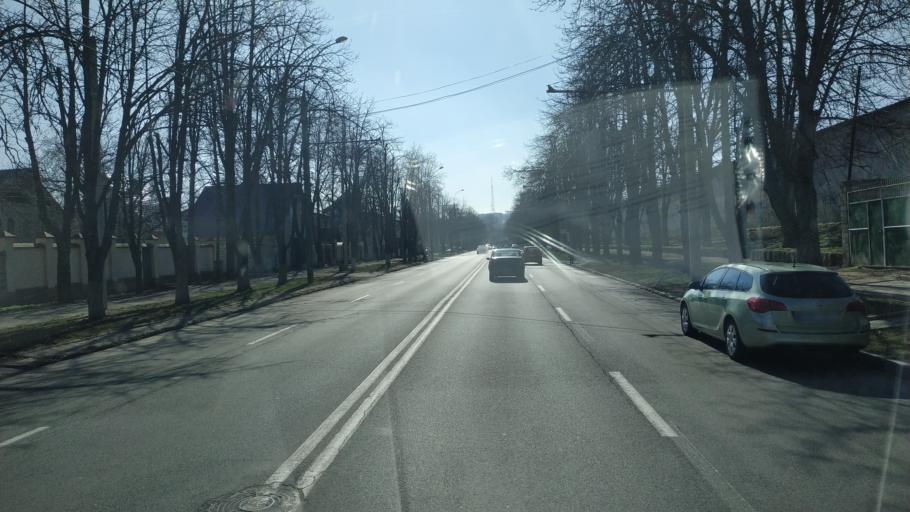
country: MD
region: Chisinau
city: Chisinau
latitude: 47.0255
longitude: 28.8029
